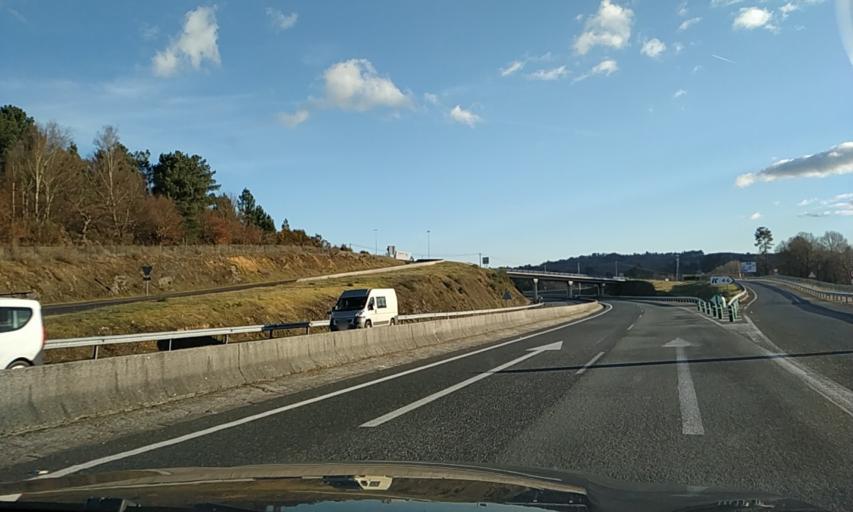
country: ES
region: Galicia
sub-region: Provincia de Pontevedra
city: Lalin
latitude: 42.6407
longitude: -8.1325
